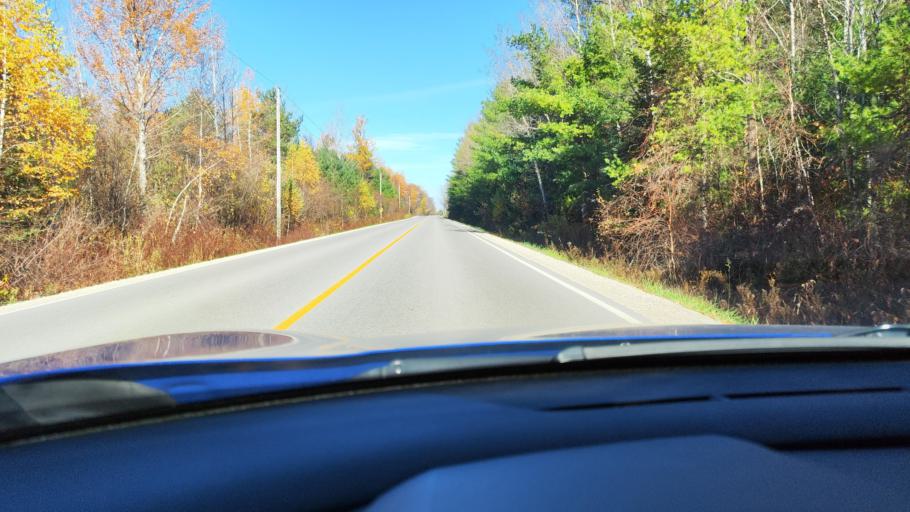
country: CA
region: Ontario
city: Wasaga Beach
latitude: 44.4066
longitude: -80.0592
